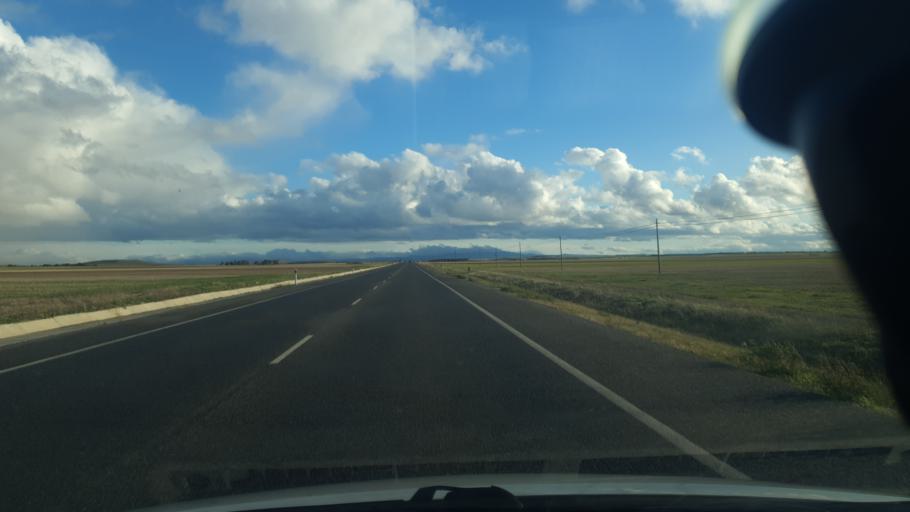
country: ES
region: Castille and Leon
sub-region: Provincia de Segovia
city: Codorniz
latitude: 41.0335
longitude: -4.6195
